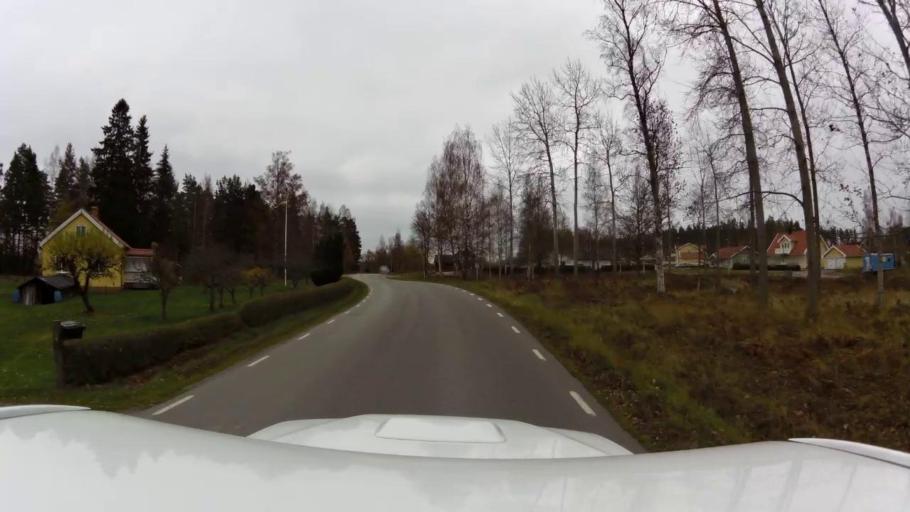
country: SE
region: OEstergoetland
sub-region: Kinda Kommun
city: Rimforsa
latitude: 58.1428
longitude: 15.6679
